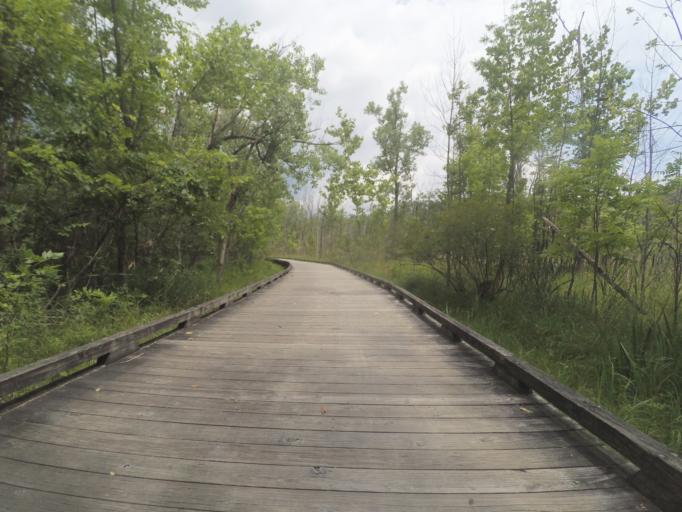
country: US
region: Ohio
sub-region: Summit County
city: Peninsula
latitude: 41.2528
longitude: -81.5453
